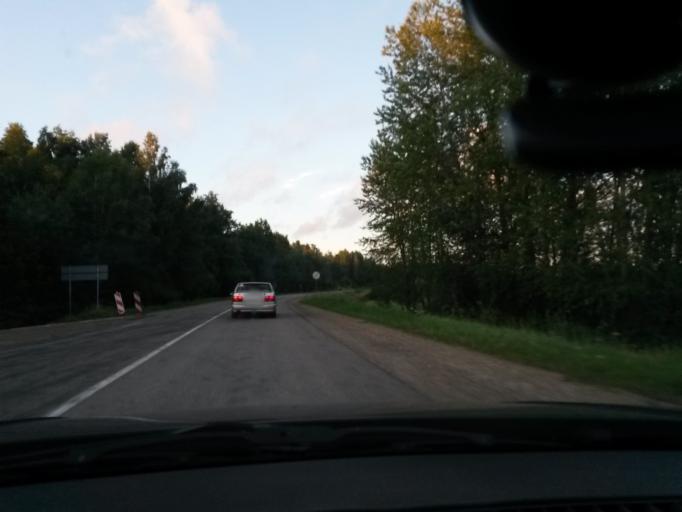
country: LV
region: Madonas Rajons
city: Madona
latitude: 56.8051
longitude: 26.0447
